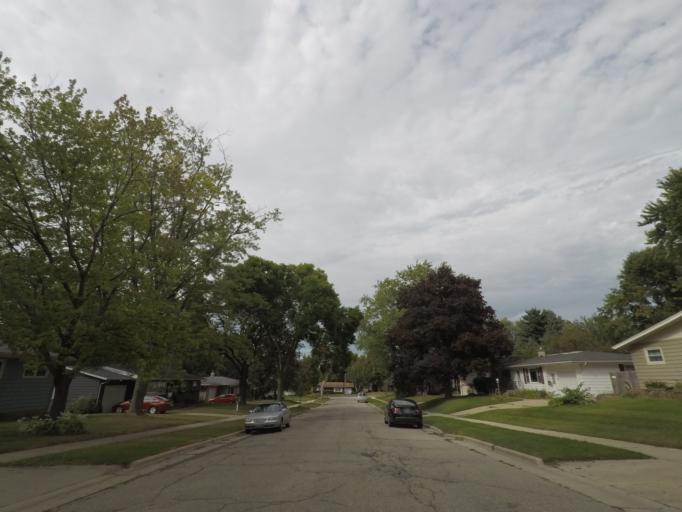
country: US
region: Wisconsin
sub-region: Dane County
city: Monona
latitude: 43.0757
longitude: -89.3020
